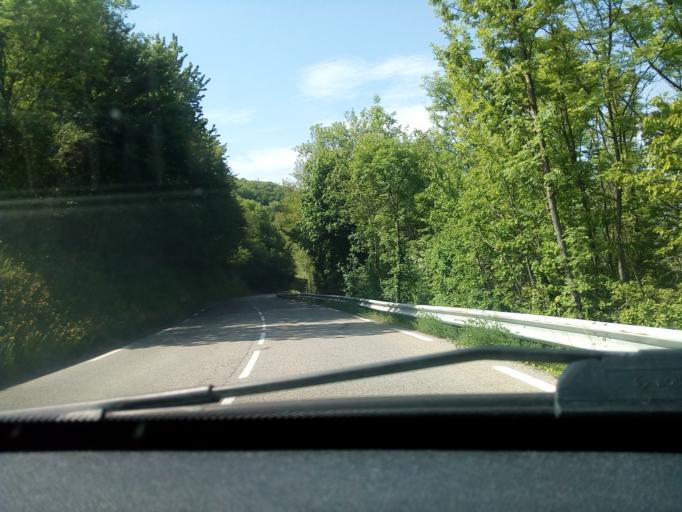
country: FR
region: Rhone-Alpes
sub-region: Departement de l'Isere
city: Le Champ-pres-Froges
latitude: 45.2812
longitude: 5.9372
